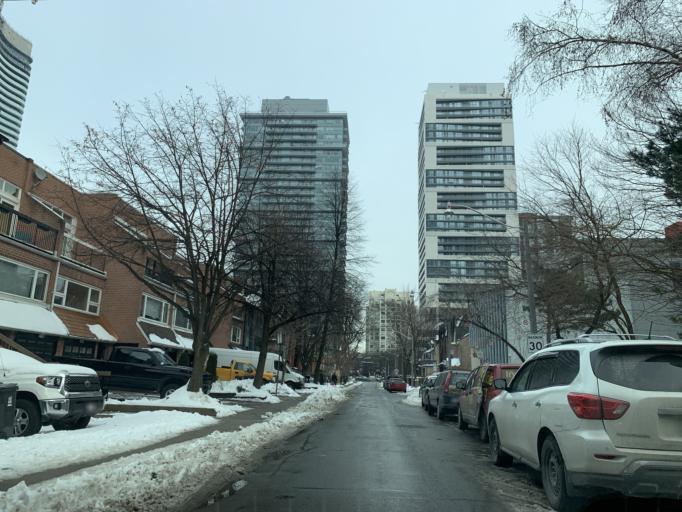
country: CA
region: Ontario
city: Toronto
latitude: 43.6603
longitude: -79.3807
